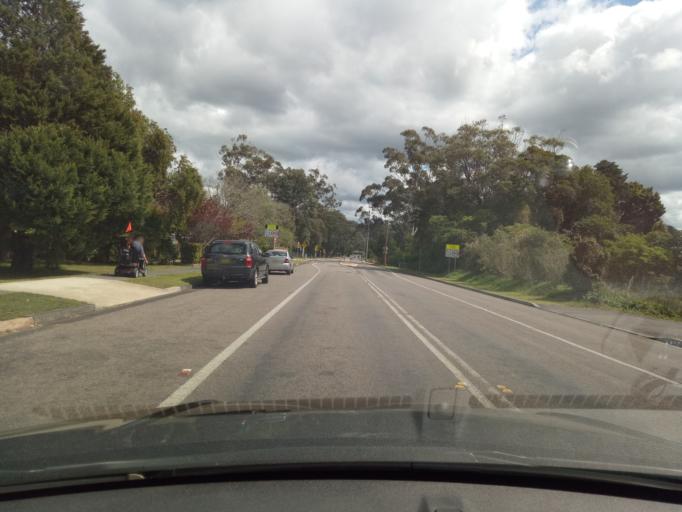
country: AU
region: New South Wales
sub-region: Gosford Shire
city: Lisarow
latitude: -33.3850
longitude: 151.3733
